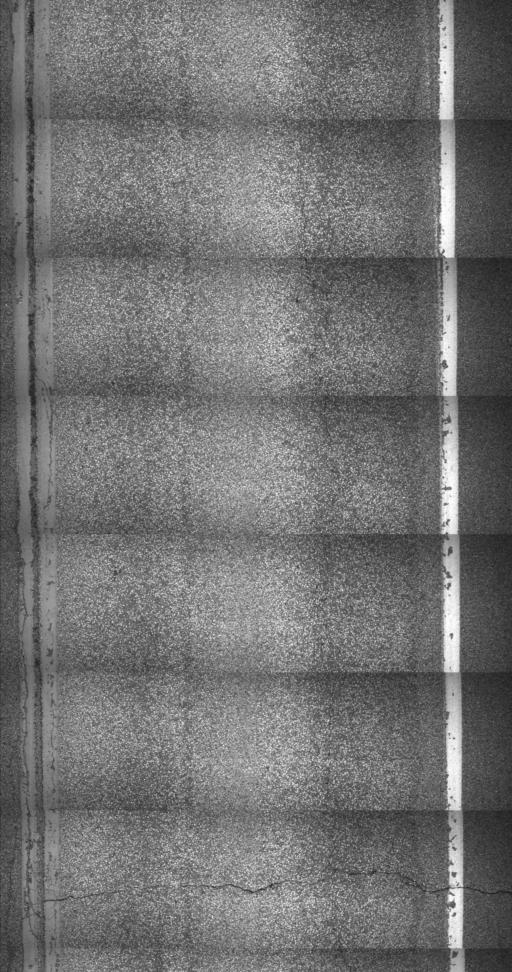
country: US
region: Vermont
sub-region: Washington County
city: Montpelier
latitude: 44.3969
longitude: -72.5559
